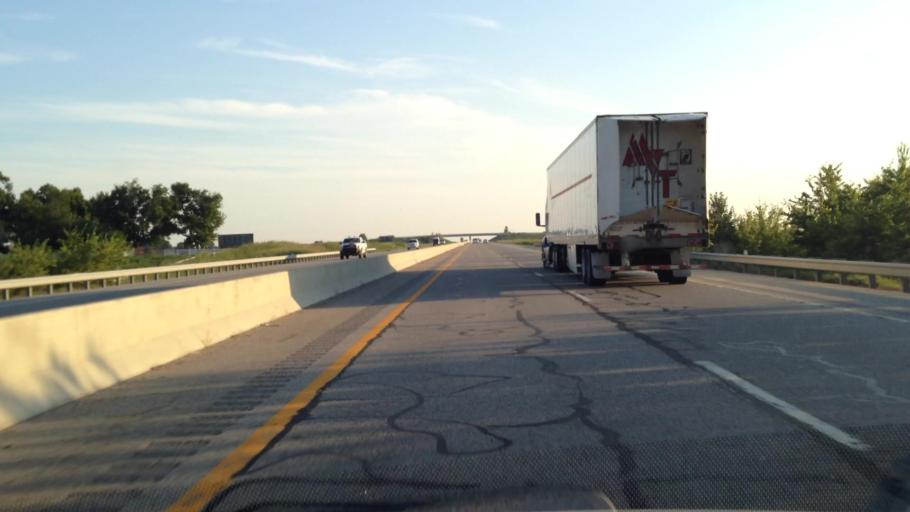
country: US
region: Oklahoma
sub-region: Ottawa County
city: Fairland
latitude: 36.8090
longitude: -94.8766
